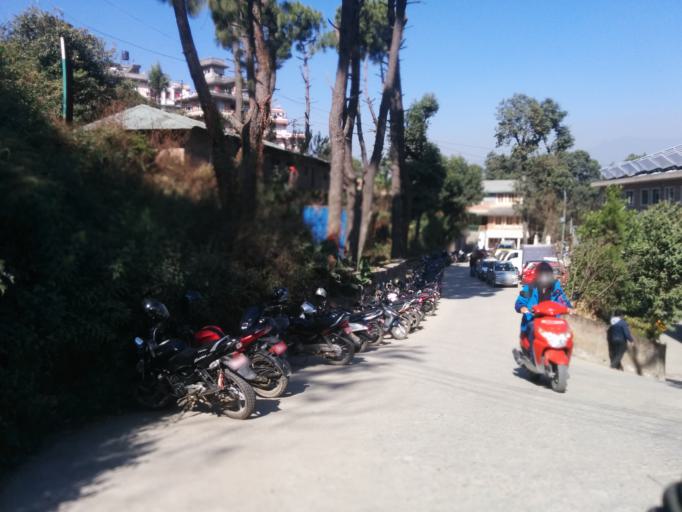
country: NP
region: Central Region
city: Kirtipur
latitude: 27.6822
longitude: 85.2736
